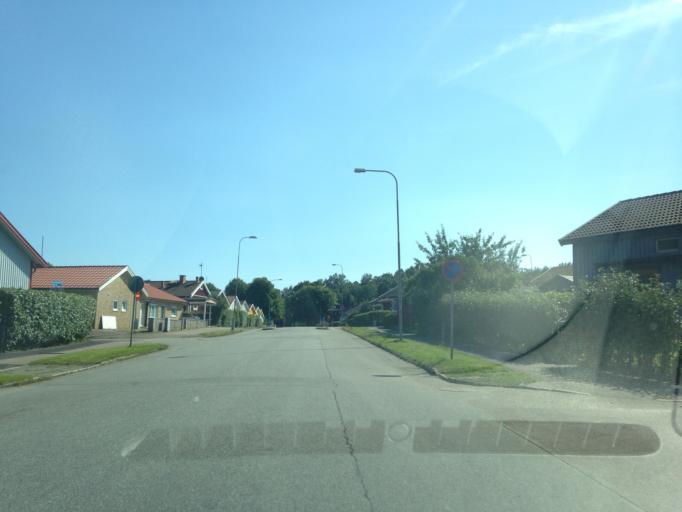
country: SE
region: Vaestra Goetaland
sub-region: Goteborg
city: Majorna
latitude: 57.7270
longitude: 11.9175
